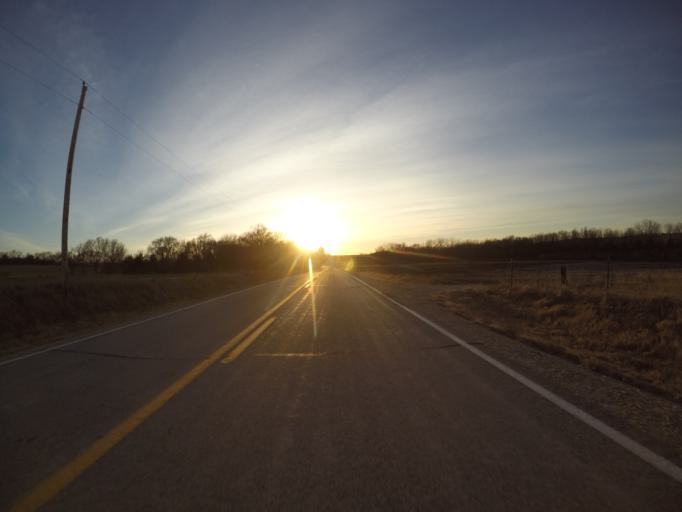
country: US
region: Kansas
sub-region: Clay County
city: Clay Center
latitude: 39.4371
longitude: -96.8557
